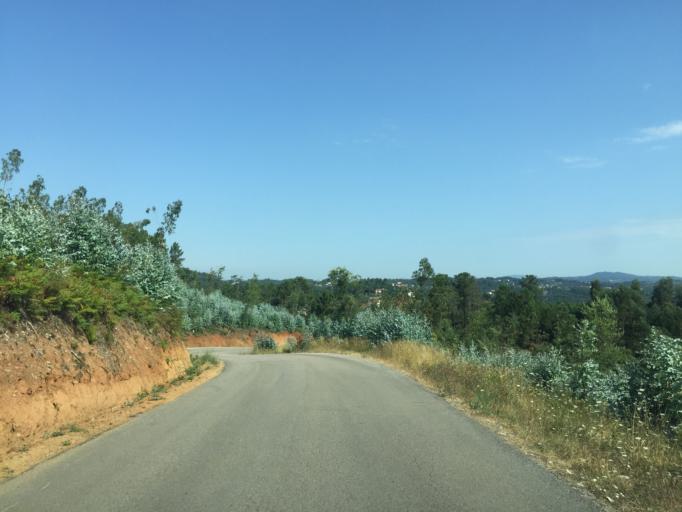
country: PT
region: Santarem
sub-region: Ferreira do Zezere
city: Ferreira do Zezere
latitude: 39.6006
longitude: -8.2928
